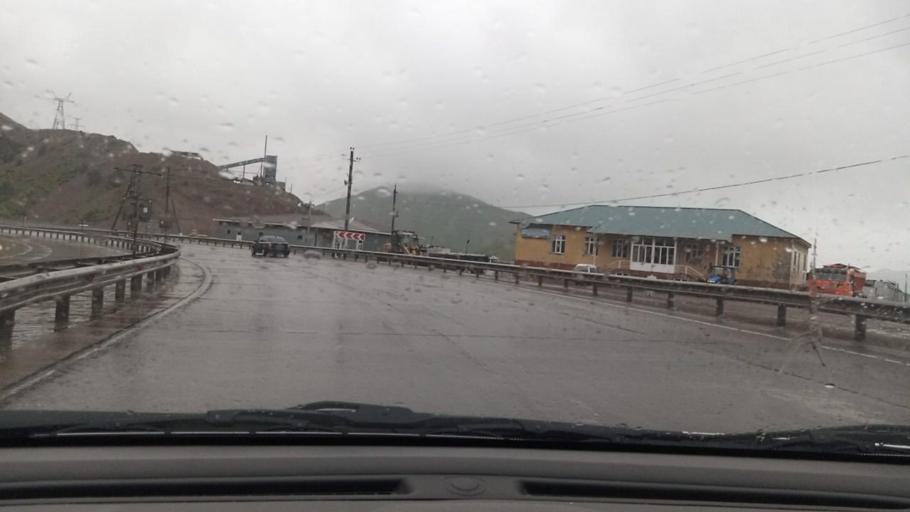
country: UZ
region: Toshkent
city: Angren
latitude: 41.0913
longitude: 70.5319
